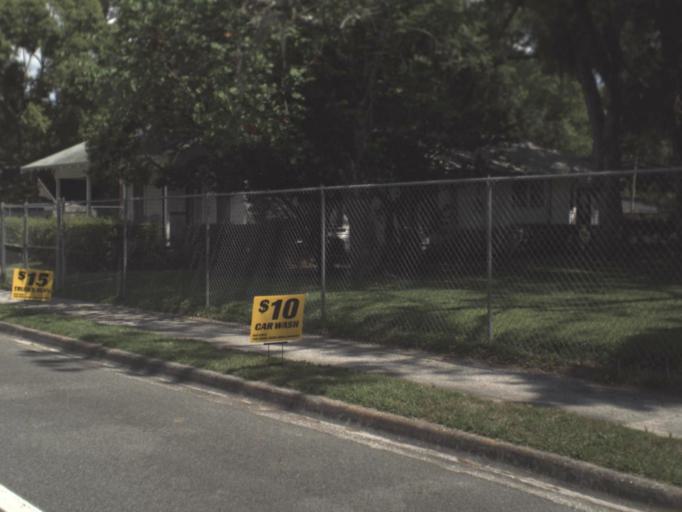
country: US
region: Florida
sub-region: Bradford County
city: Starke
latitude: 29.9499
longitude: -82.1043
